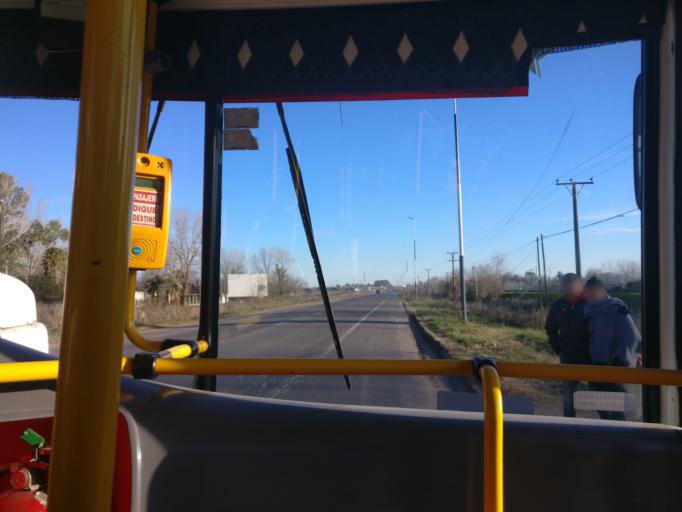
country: AR
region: Buenos Aires
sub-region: Partido de Ezeiza
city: Ezeiza
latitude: -34.9221
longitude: -58.6077
